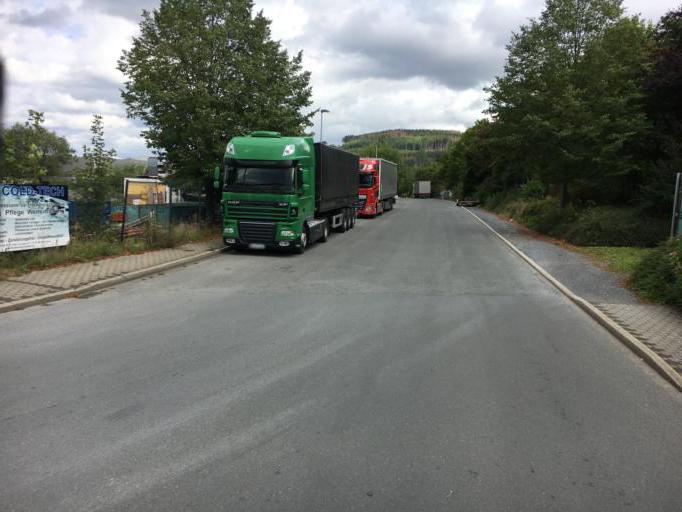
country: DE
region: North Rhine-Westphalia
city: Plettenberg
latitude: 51.1966
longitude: 7.8375
